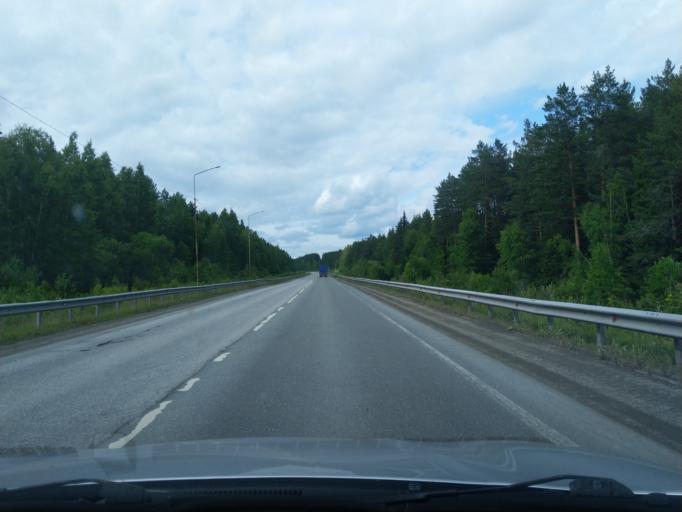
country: RU
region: Sverdlovsk
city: Nizhniy Tagil
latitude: 57.9522
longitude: 59.8722
